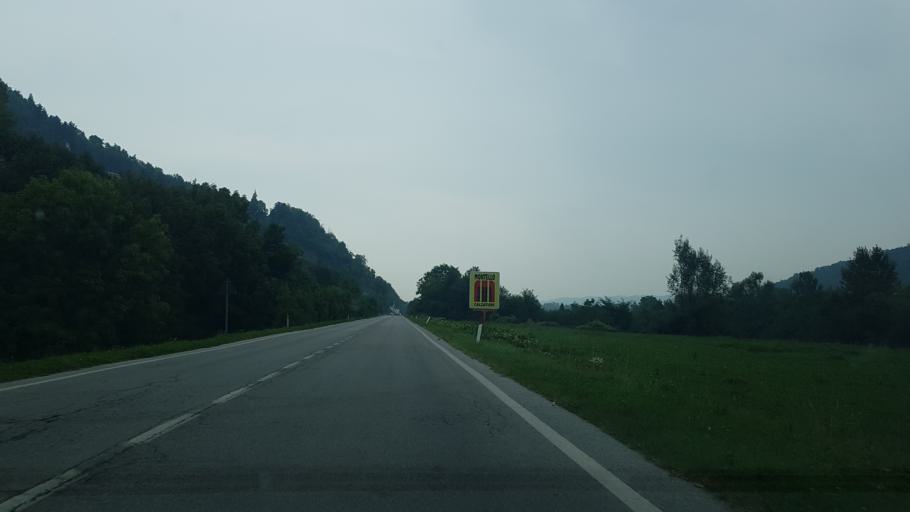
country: IT
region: Piedmont
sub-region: Provincia di Cuneo
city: Roccaforte Mondovi
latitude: 44.3283
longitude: 7.7508
